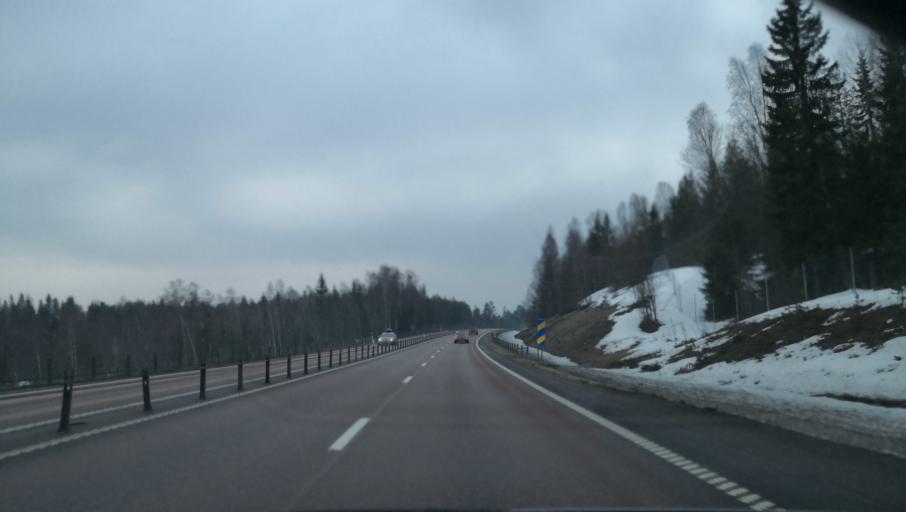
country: SE
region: Gaevleborg
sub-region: Hudiksvalls Kommun
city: Hudiksvall
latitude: 61.8617
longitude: 17.2060
